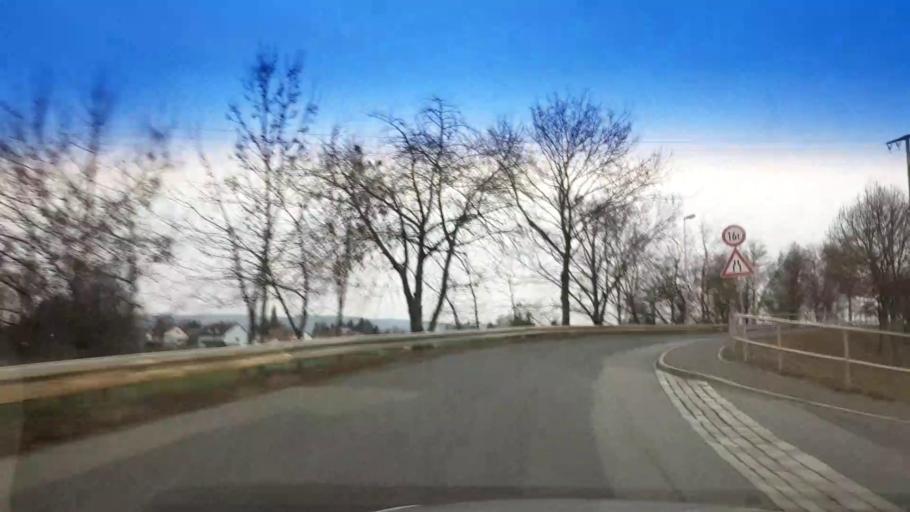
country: DE
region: Bavaria
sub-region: Upper Franconia
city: Altendorf
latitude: 49.7943
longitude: 11.0053
